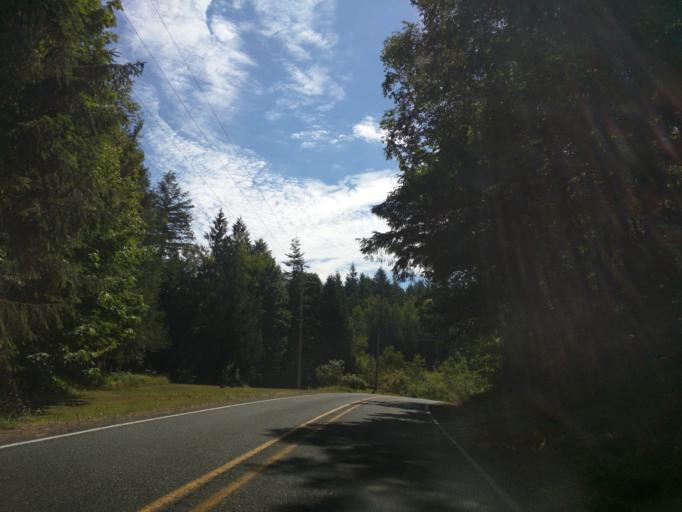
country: US
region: Washington
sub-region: Whatcom County
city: Peaceful Valley
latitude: 48.9707
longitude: -122.1664
